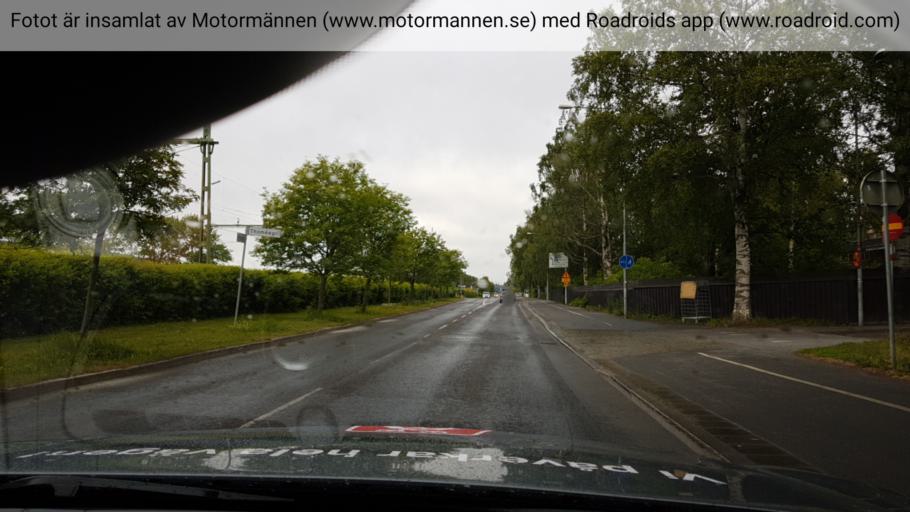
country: SE
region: Jaemtland
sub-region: OEstersunds Kommun
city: Ostersund
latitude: 63.1747
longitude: 14.6322
